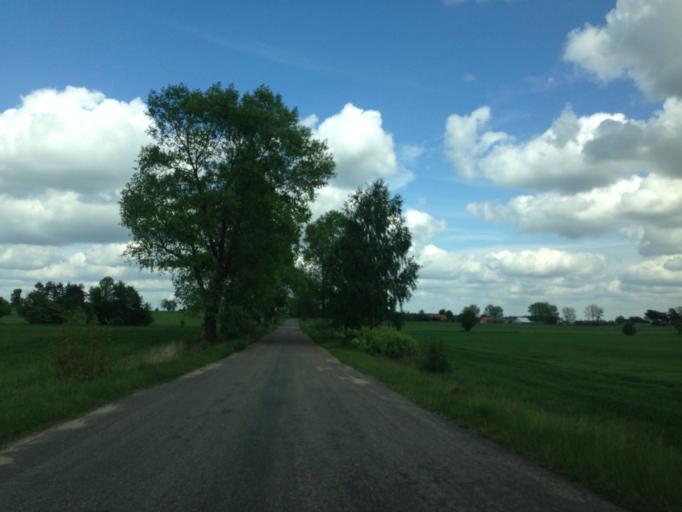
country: PL
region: Warmian-Masurian Voivodeship
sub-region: Powiat nidzicki
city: Kozlowo
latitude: 53.3994
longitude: 20.2272
